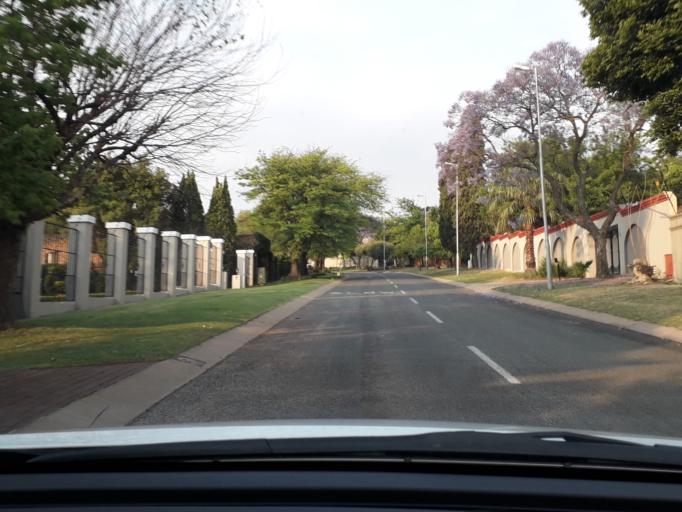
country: ZA
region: Gauteng
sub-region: City of Johannesburg Metropolitan Municipality
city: Modderfontein
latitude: -26.0764
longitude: 28.0755
